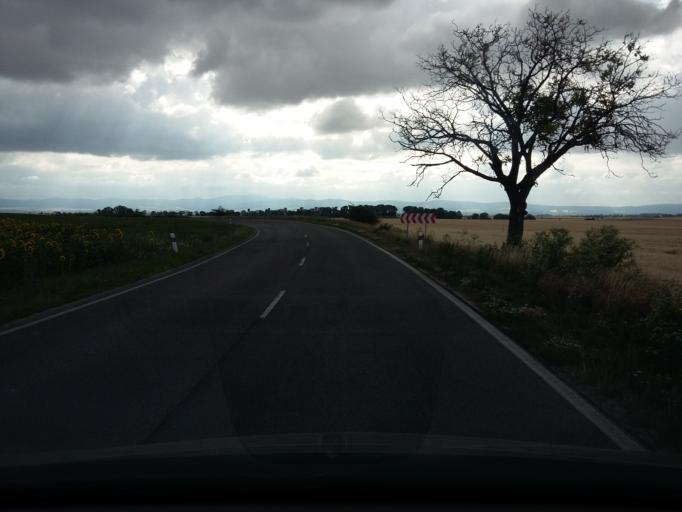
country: SK
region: Trnavsky
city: Vrbove
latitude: 48.6009
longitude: 17.6972
